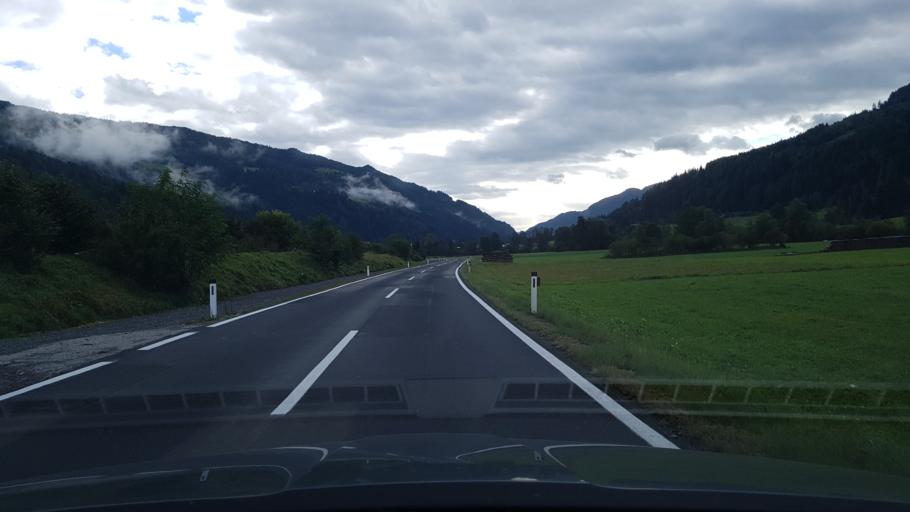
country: AT
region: Styria
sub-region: Politischer Bezirk Murau
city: Winklern bei Oberwolz
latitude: 47.1805
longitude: 14.2125
